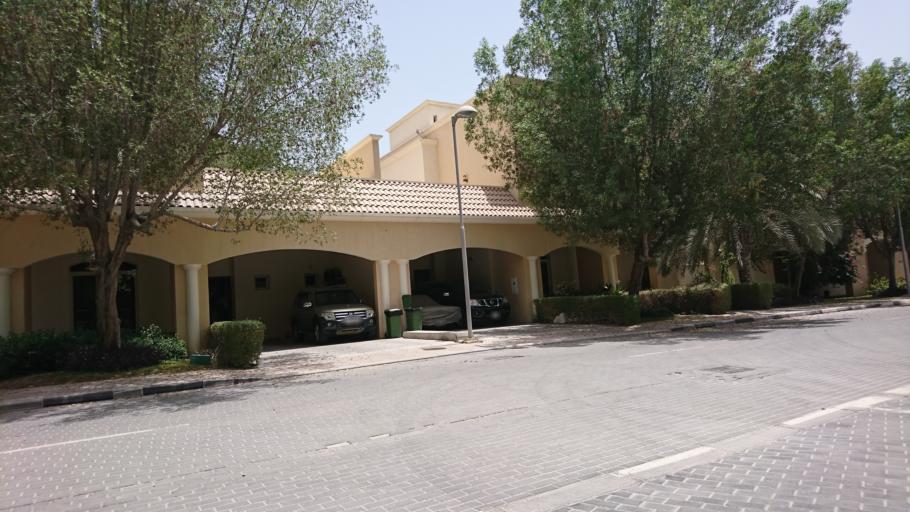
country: QA
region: Baladiyat ad Dawhah
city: Doha
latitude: 25.3836
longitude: 51.5161
